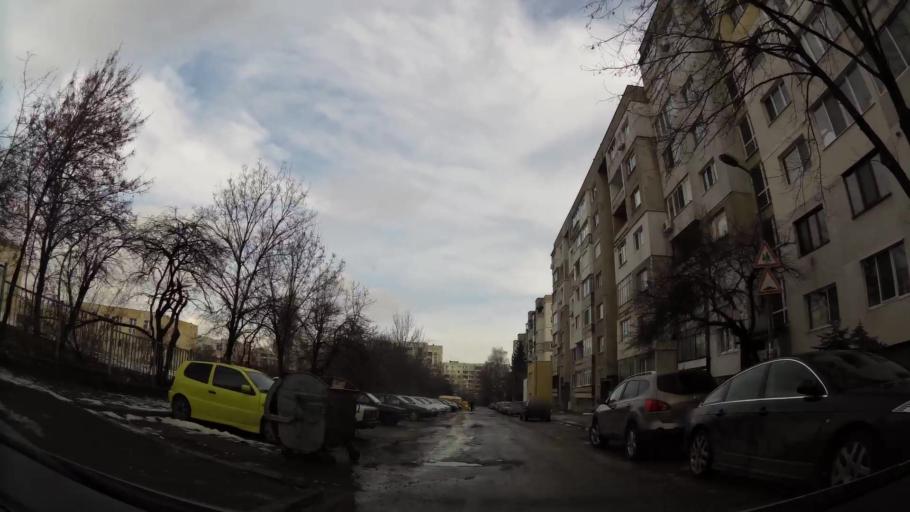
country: BG
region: Sofiya
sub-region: Obshtina Bozhurishte
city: Bozhurishte
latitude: 42.7188
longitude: 23.2482
